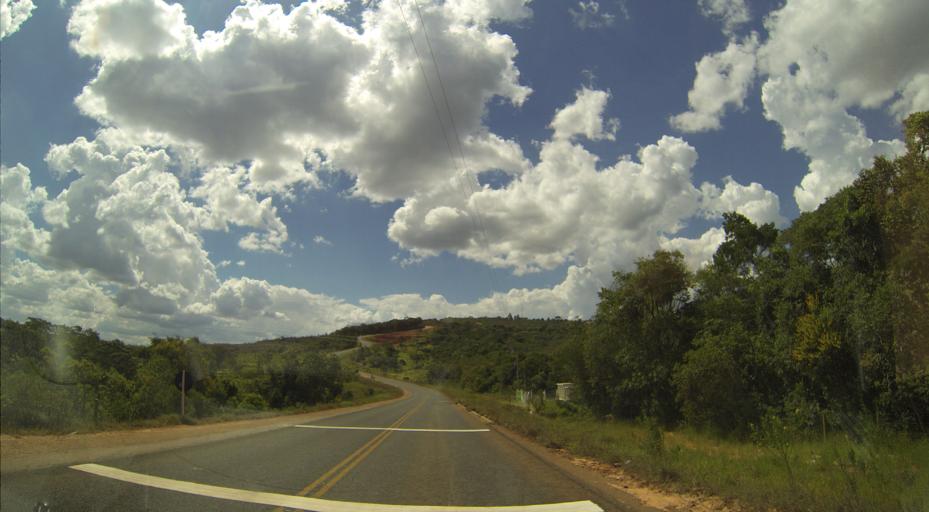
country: BR
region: Minas Gerais
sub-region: Serro
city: Serro
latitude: -18.4827
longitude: -43.4924
